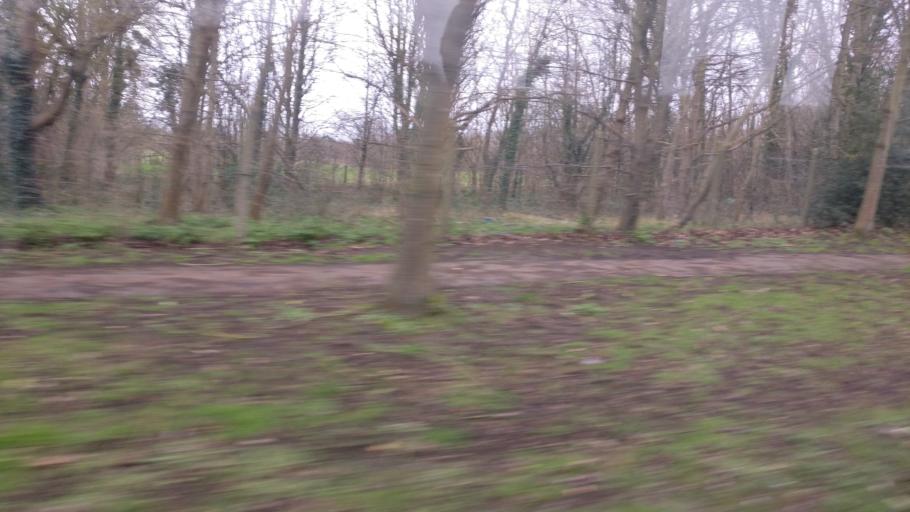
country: GB
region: England
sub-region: Surrey
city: Staines
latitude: 51.4109
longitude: -0.5089
